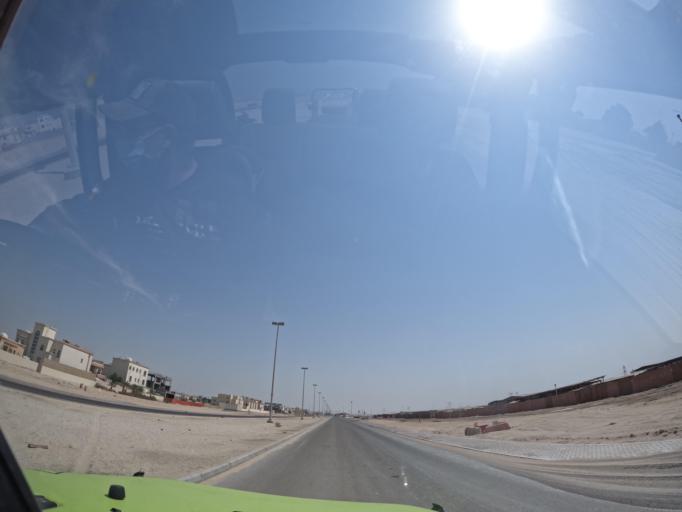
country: AE
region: Abu Dhabi
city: Abu Dhabi
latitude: 24.3045
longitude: 54.5381
